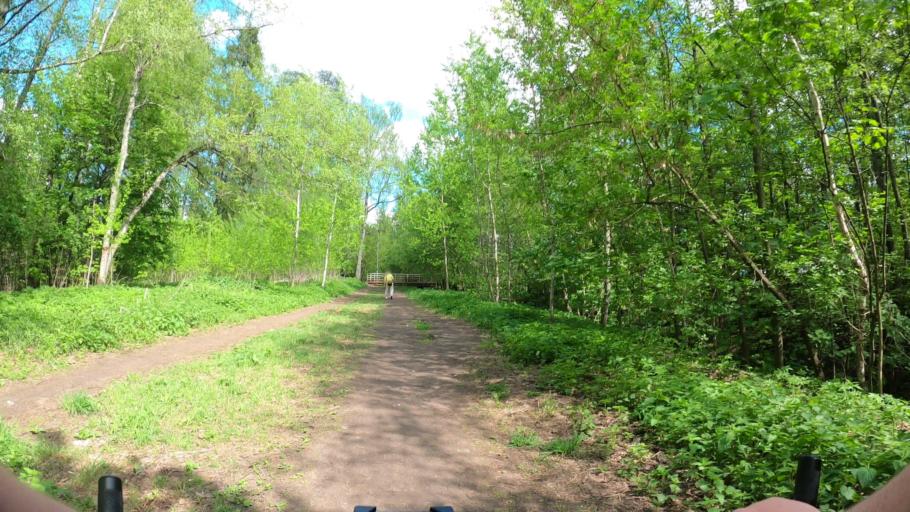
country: RU
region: Moskovskaya
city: Ramenskoye
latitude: 55.5790
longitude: 38.2237
